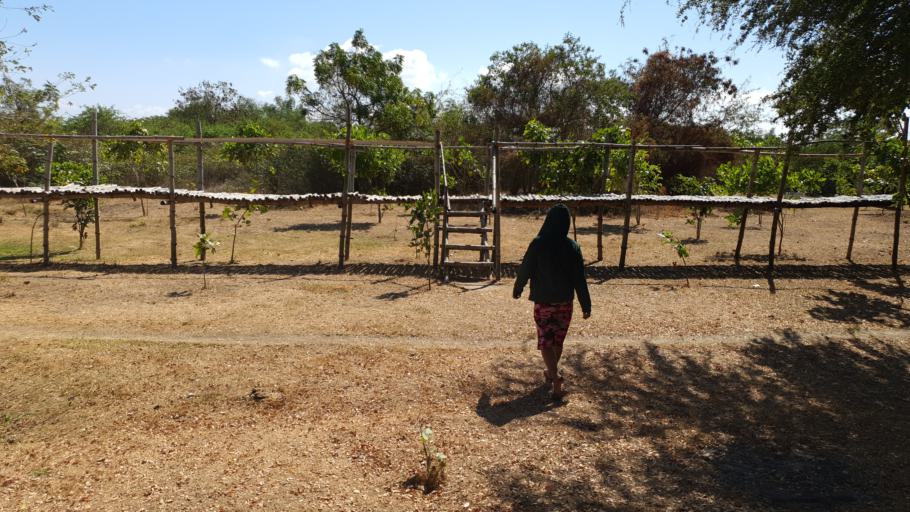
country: PH
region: Ilocos
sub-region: Province of La Union
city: Payocpoc Sur
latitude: 16.5045
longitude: 120.3111
